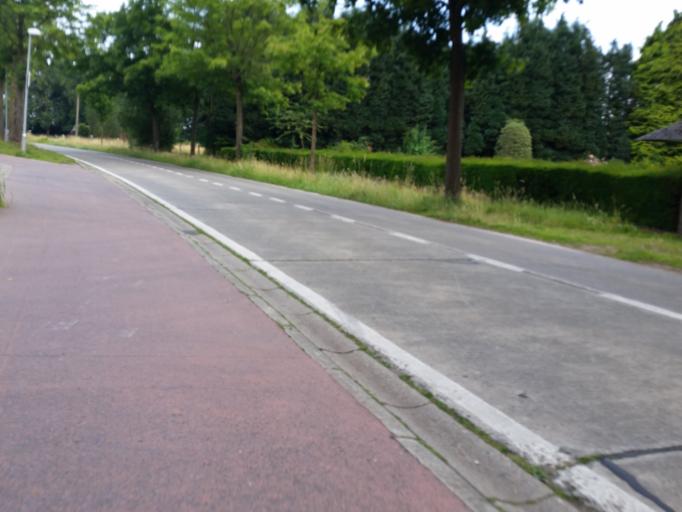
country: BE
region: Flanders
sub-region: Provincie Antwerpen
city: Puurs
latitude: 51.0603
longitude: 4.3154
